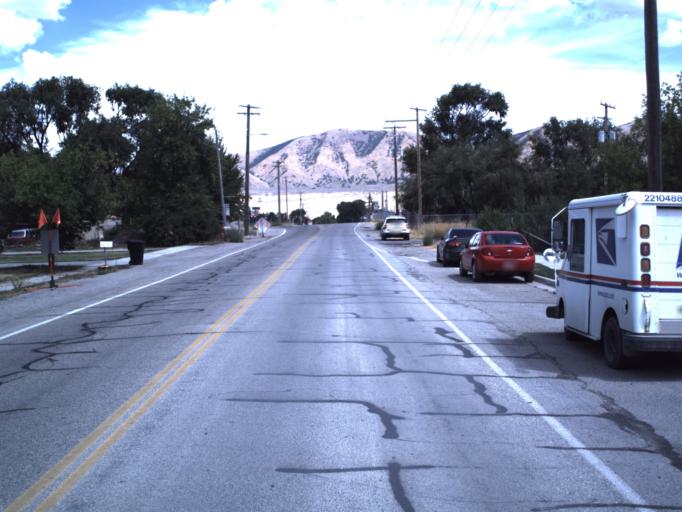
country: US
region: Utah
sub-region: Box Elder County
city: Garland
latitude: 41.7414
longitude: -112.1508
